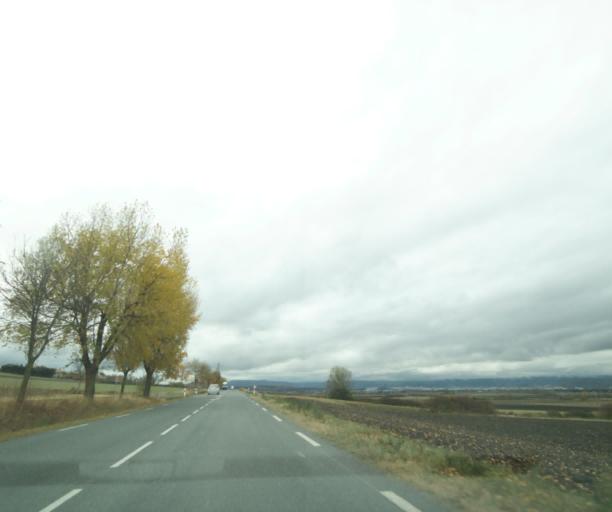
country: FR
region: Auvergne
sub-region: Departement du Puy-de-Dome
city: Pont-du-Chateau
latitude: 45.8094
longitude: 3.2328
